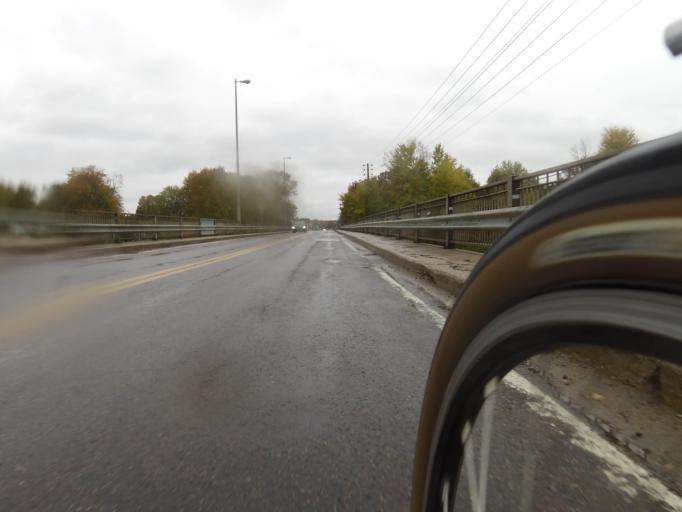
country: CA
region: Quebec
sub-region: Outaouais
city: Fort-Coulonge
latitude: 45.8505
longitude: -76.7288
